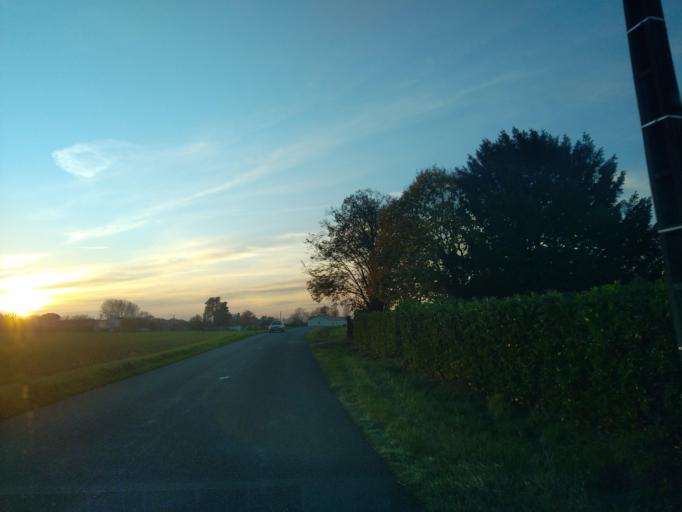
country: FR
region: Pays de la Loire
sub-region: Departement de la Vendee
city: Vix
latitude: 46.3963
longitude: -0.8286
